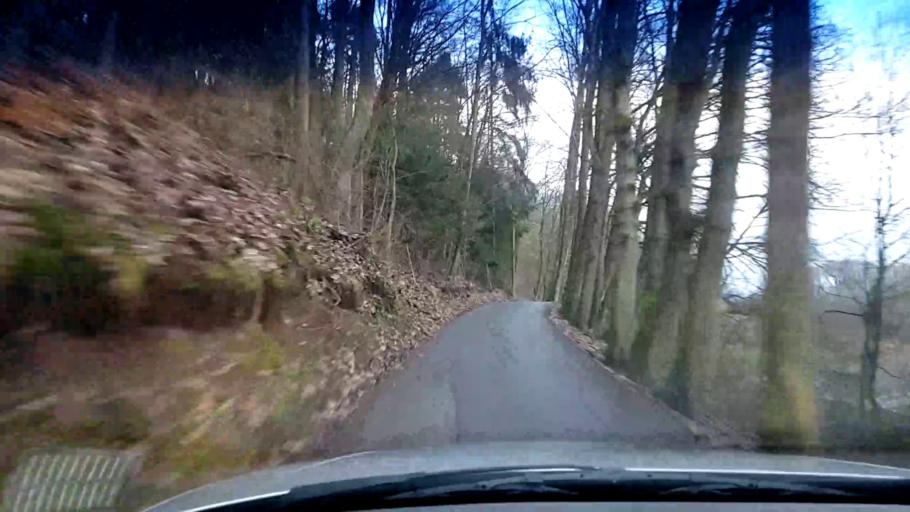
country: DE
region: Bavaria
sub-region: Upper Franconia
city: Hallstadt
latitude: 49.9374
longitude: 10.8654
